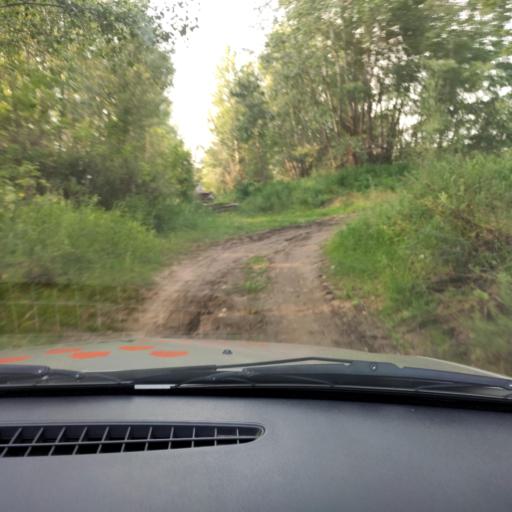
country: RU
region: Bashkortostan
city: Ufa
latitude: 54.6074
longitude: 55.9696
